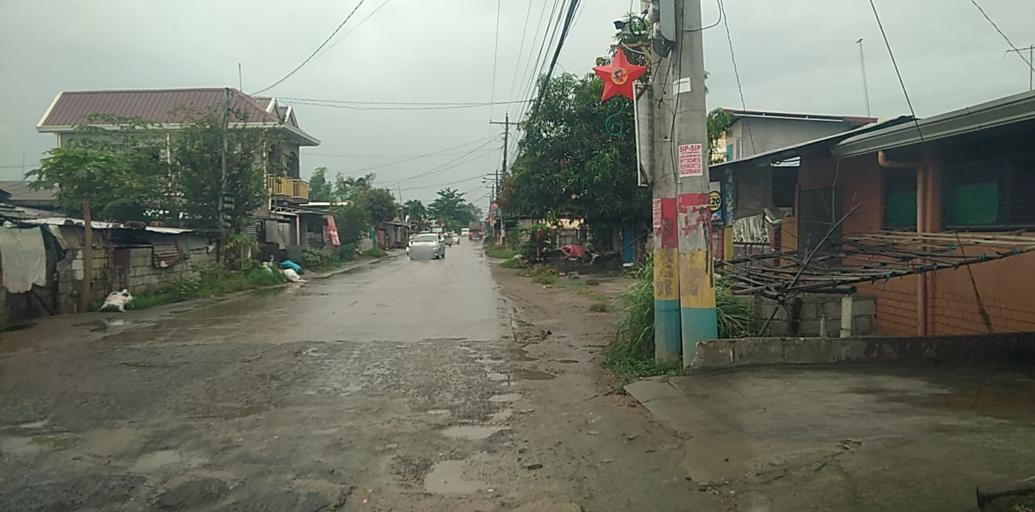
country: PH
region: Central Luzon
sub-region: Province of Pampanga
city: San Antonio
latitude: 15.1582
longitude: 120.6863
